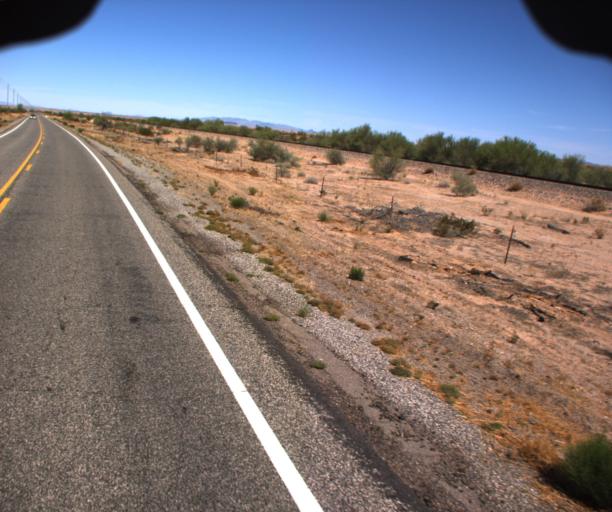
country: US
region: Arizona
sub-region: La Paz County
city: Cienega Springs
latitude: 33.9744
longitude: -114.0464
